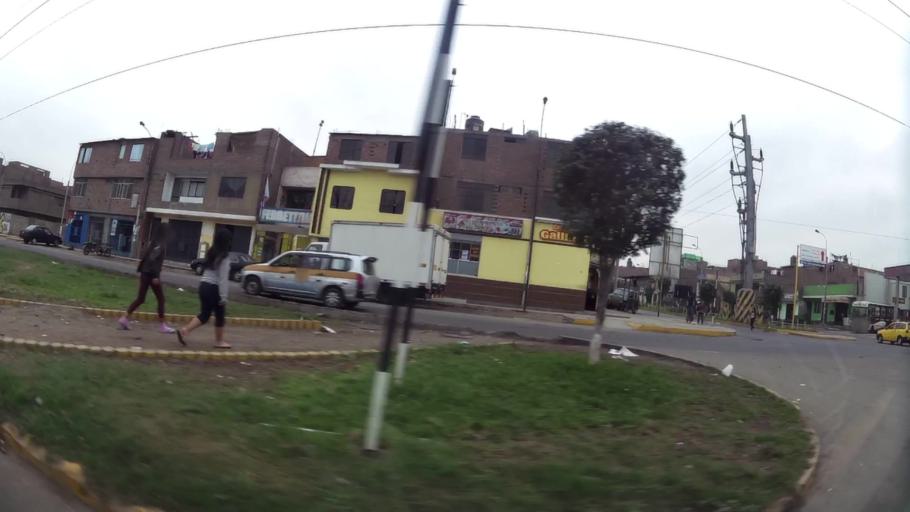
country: PE
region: Lima
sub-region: Lima
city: Vitarte
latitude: -12.0404
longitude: -76.9714
